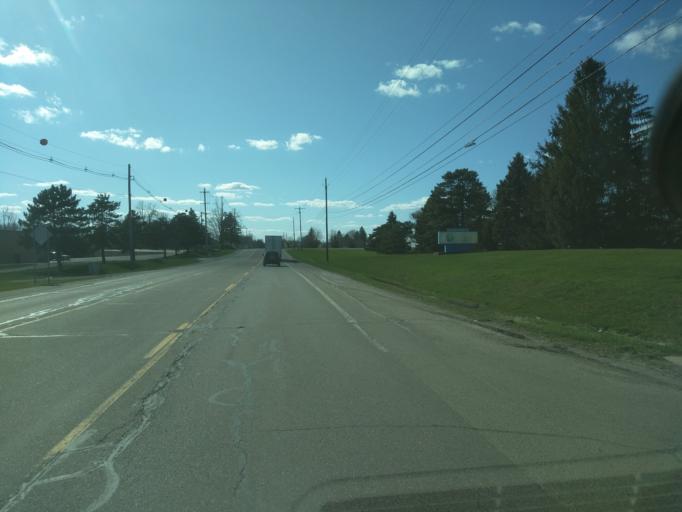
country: US
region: Michigan
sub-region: Eaton County
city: Waverly
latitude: 42.7787
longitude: -84.6374
